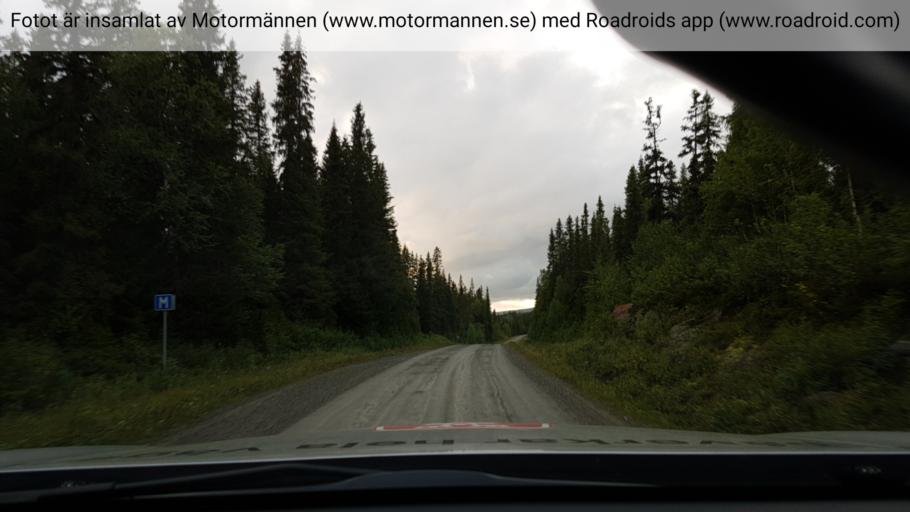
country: SE
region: Vaesterbotten
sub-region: Vilhelmina Kommun
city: Sjoberg
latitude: 65.5049
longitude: 15.4763
